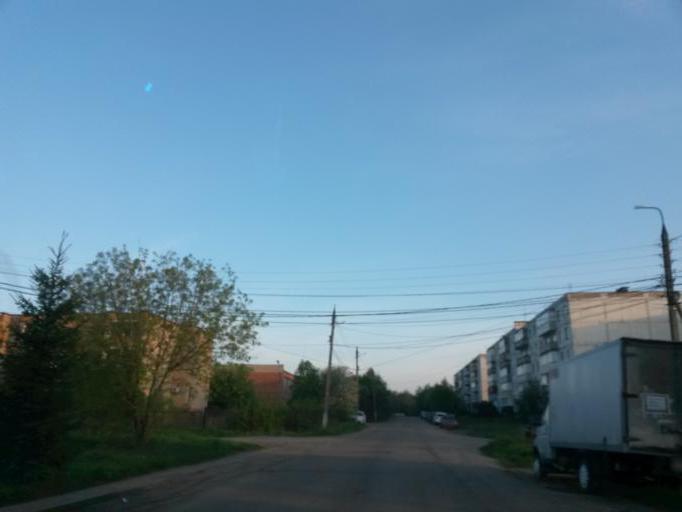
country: RU
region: Moskovskaya
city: Lyubuchany
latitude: 55.2380
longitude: 37.5423
